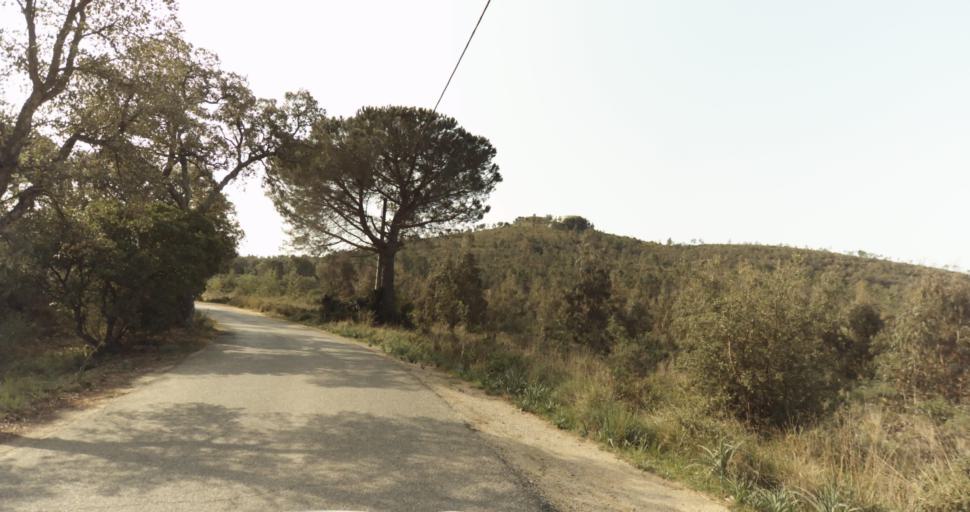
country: FR
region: Provence-Alpes-Cote d'Azur
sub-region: Departement du Var
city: Bormes-les-Mimosas
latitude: 43.1473
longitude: 6.3030
